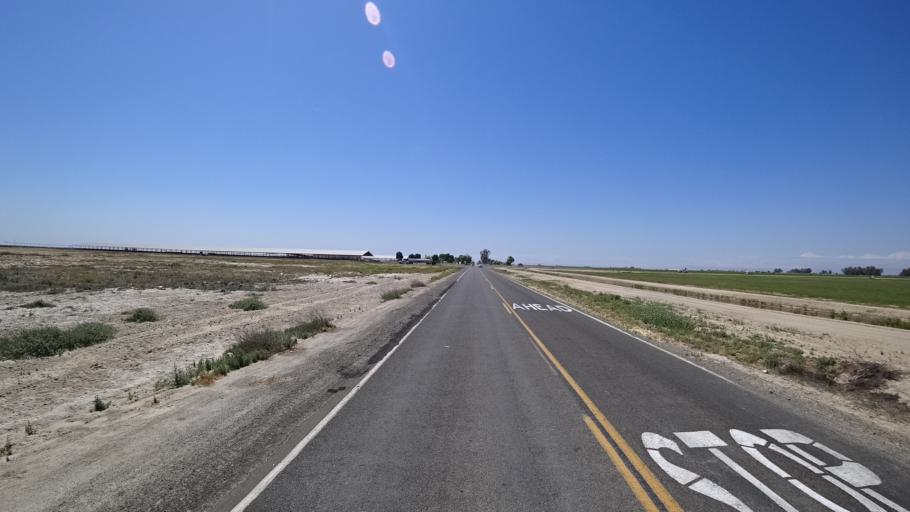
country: US
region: California
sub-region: Kings County
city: Stratford
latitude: 36.2129
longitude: -119.7623
